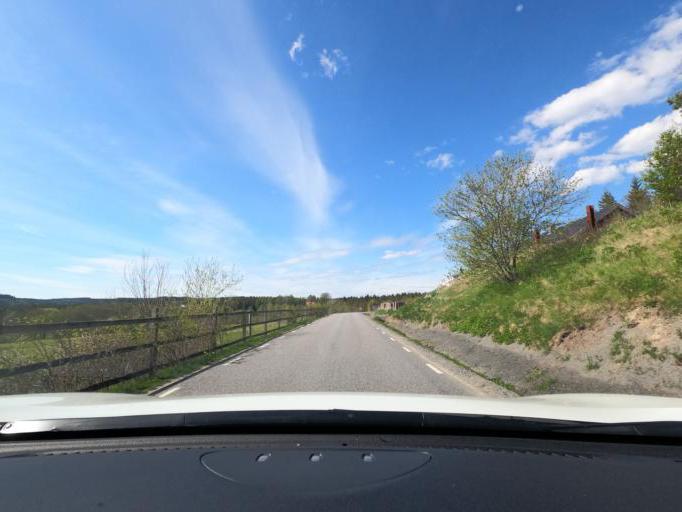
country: SE
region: Vaestra Goetaland
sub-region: Harryda Kommun
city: Ravlanda
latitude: 57.6416
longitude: 12.4972
